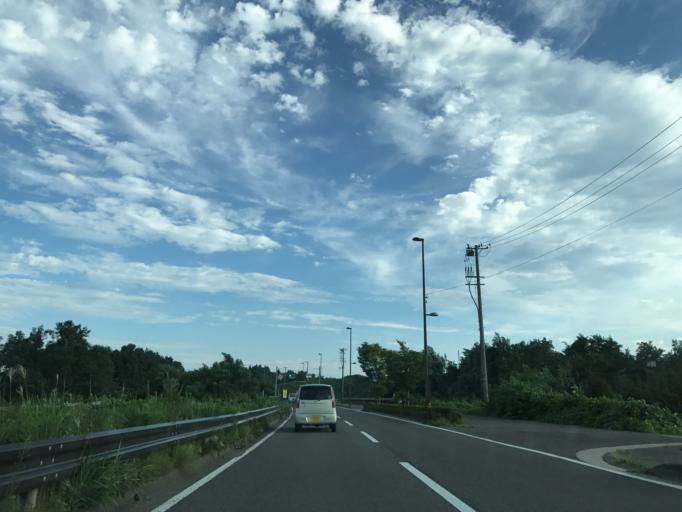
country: JP
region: Fukushima
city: Koriyama
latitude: 37.3580
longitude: 140.3255
